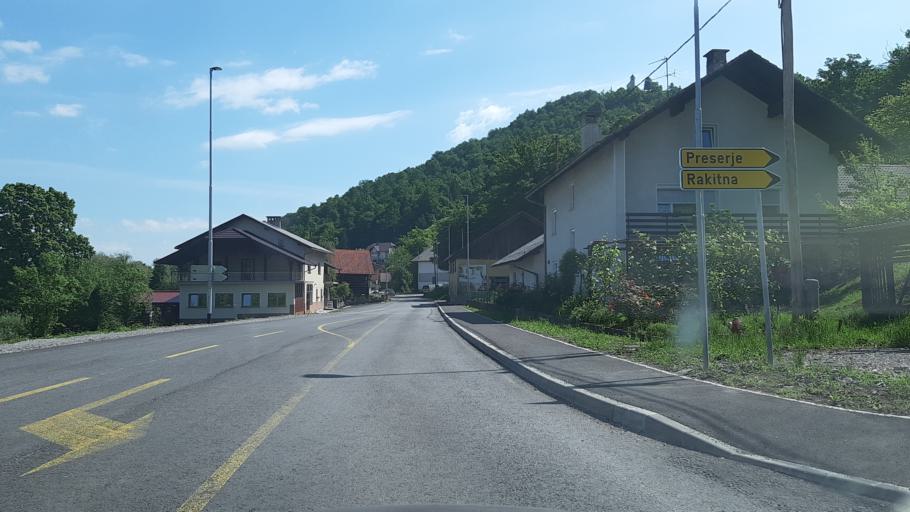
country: SI
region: Brezovica
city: Notranje Gorice
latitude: 45.9674
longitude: 14.4131
